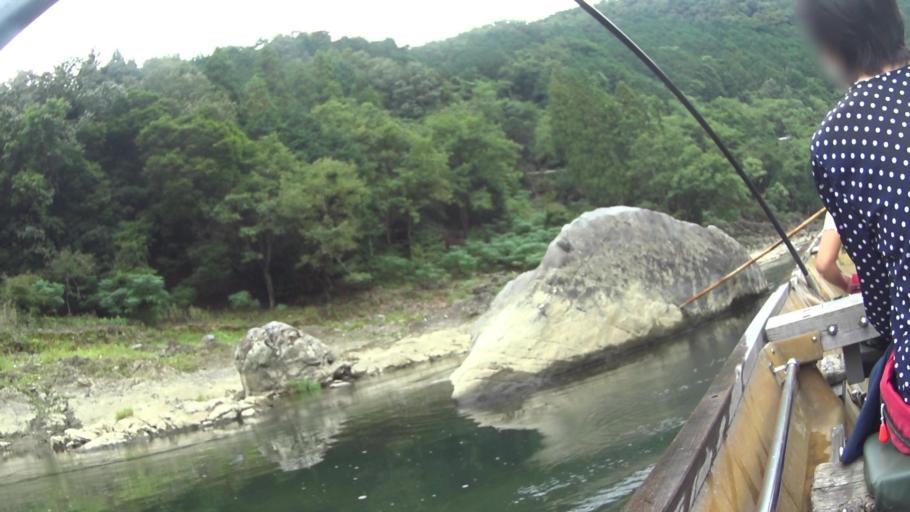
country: JP
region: Kyoto
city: Kameoka
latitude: 35.0239
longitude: 135.6196
